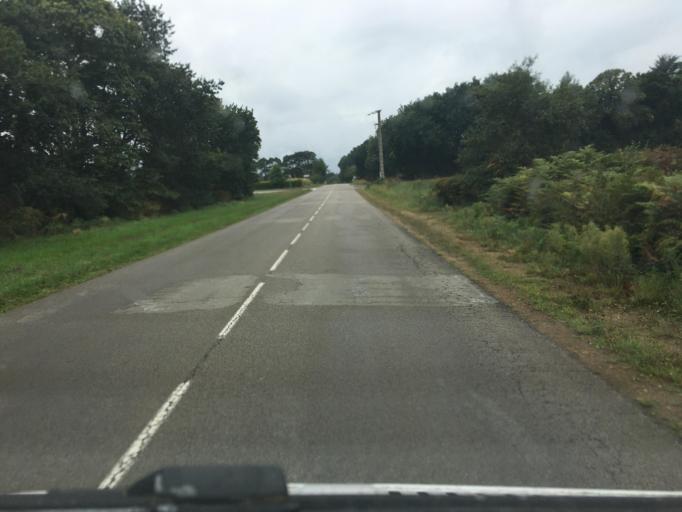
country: FR
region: Brittany
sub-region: Departement du Finistere
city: Poullan-sur-Mer
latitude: 48.0847
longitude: -4.3831
